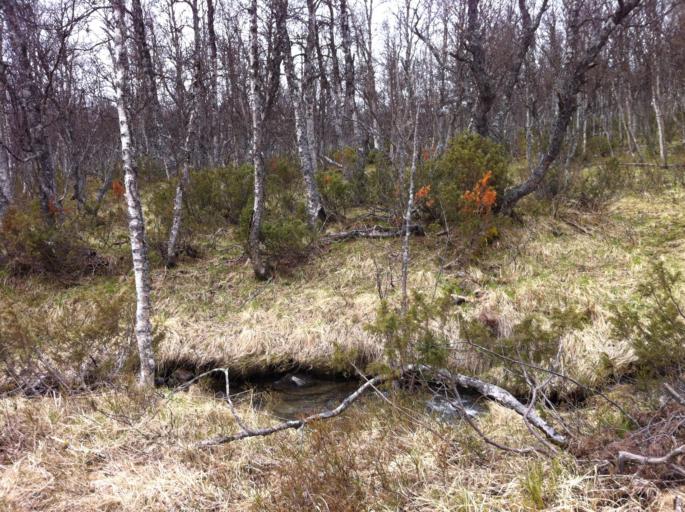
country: NO
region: Sor-Trondelag
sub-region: Tydal
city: Aas
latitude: 62.5548
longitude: 12.3125
